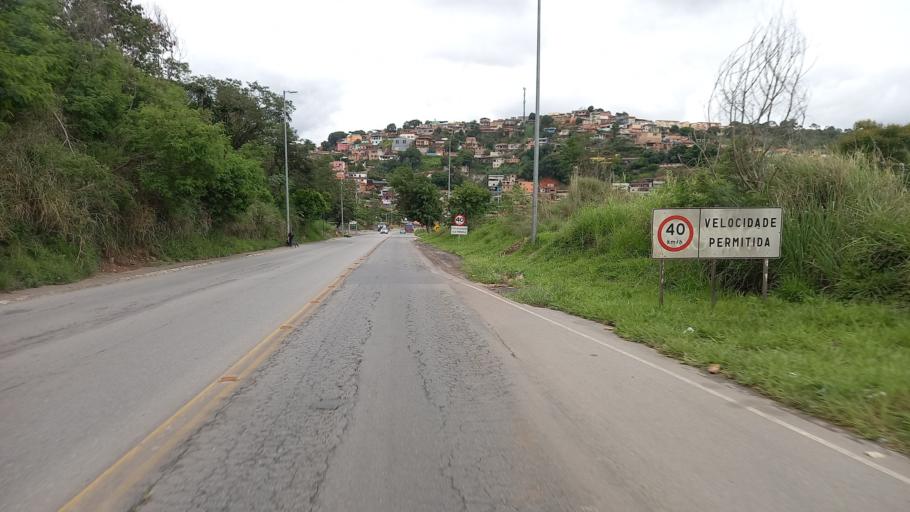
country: BR
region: Minas Gerais
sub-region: Belo Horizonte
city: Belo Horizonte
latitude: -19.8711
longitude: -43.8937
